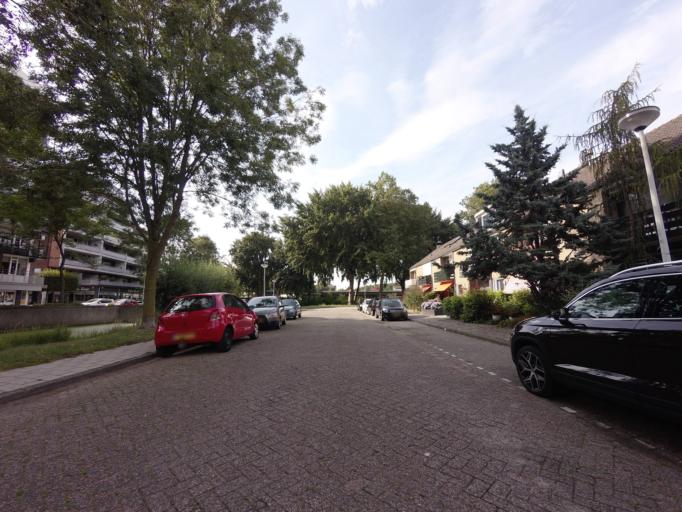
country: NL
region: South Holland
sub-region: Gemeente Papendrecht
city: Papendrecht
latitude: 51.8287
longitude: 4.7007
